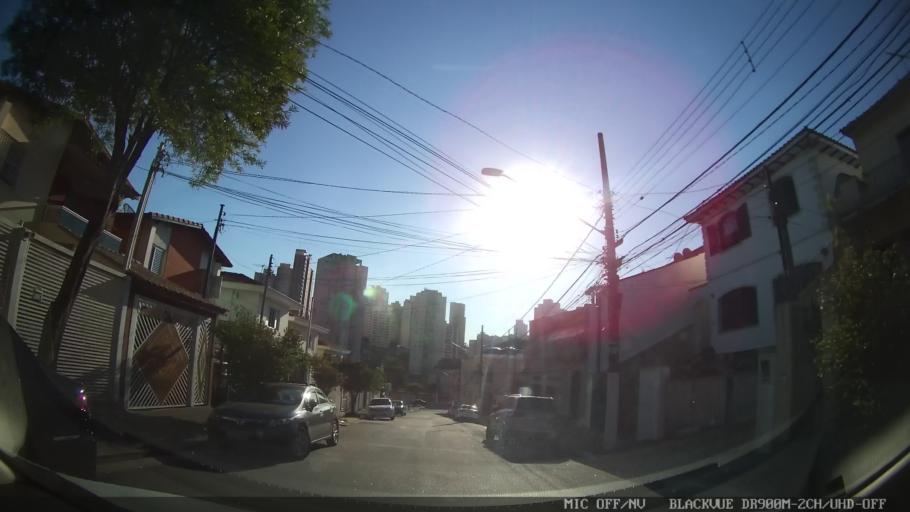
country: BR
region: Sao Paulo
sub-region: Sao Paulo
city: Sao Paulo
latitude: -23.4942
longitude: -46.6220
